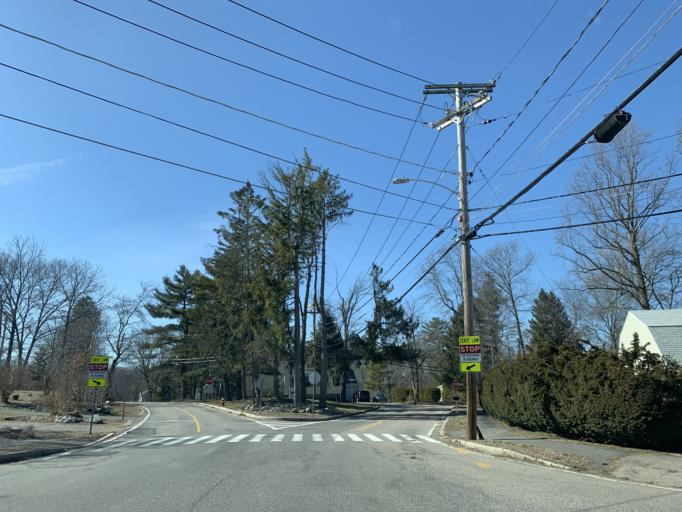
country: US
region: Massachusetts
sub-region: Norfolk County
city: Norwood
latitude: 42.1586
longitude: -71.1948
